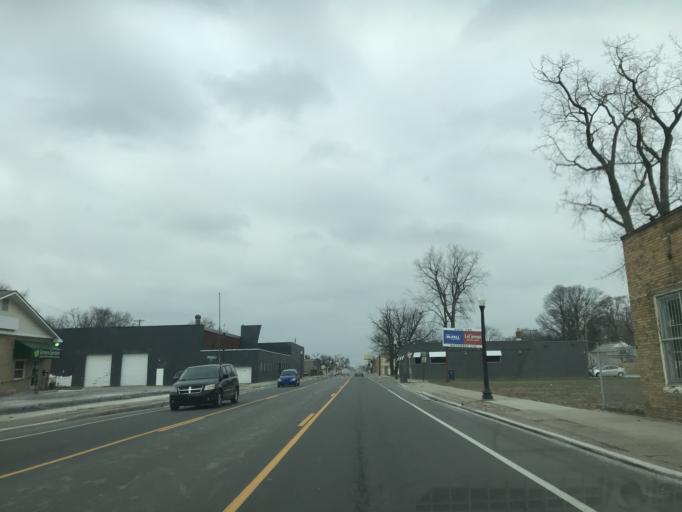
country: US
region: Michigan
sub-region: Oakland County
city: Hazel Park
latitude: 42.4502
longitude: -83.1030
